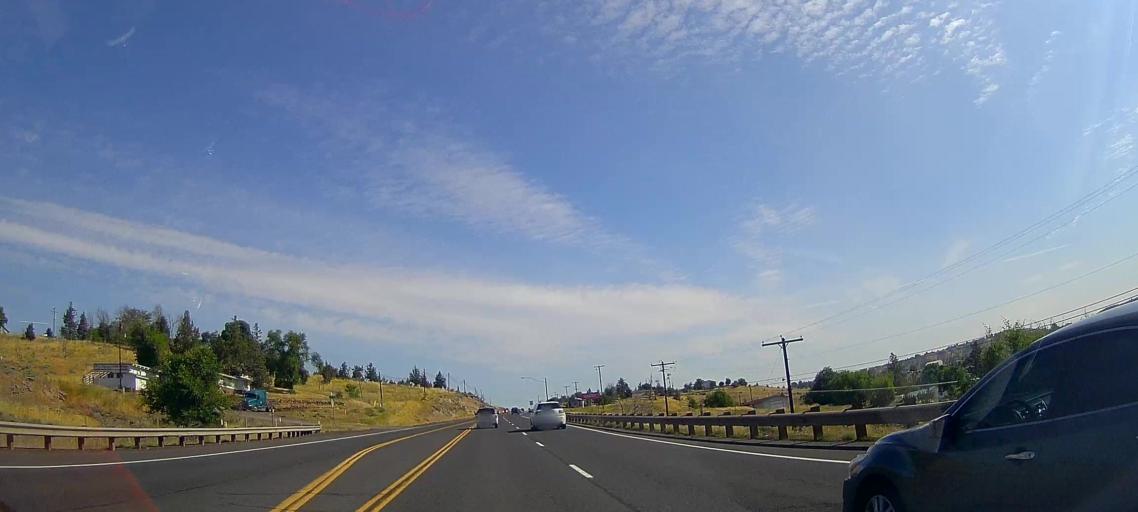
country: US
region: Oregon
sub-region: Jefferson County
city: Madras
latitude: 44.6462
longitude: -121.1294
